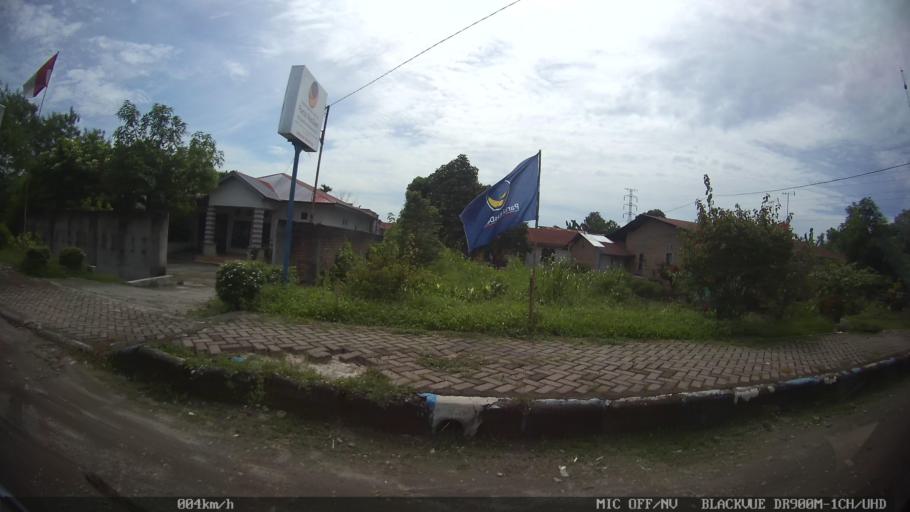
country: ID
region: North Sumatra
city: Percut
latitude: 3.6016
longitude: 98.8075
